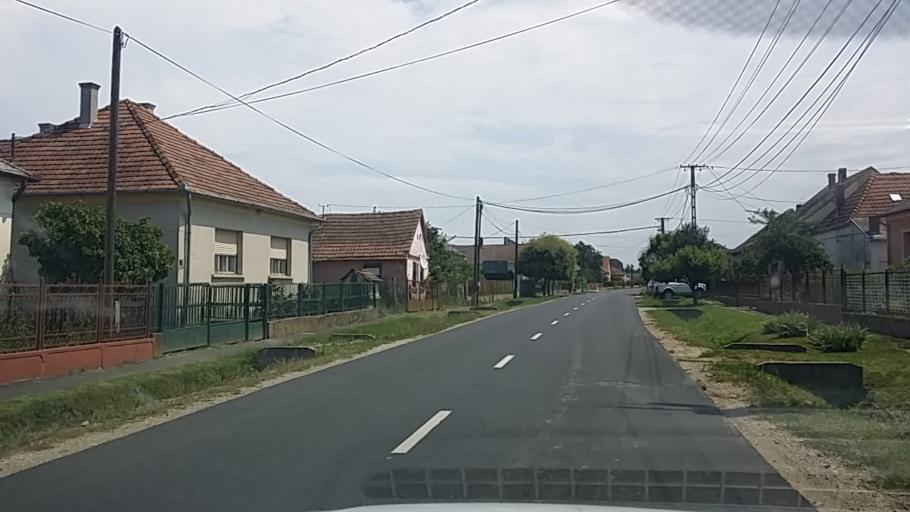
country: HU
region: Zala
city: Letenye
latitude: 46.4205
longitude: 16.7487
